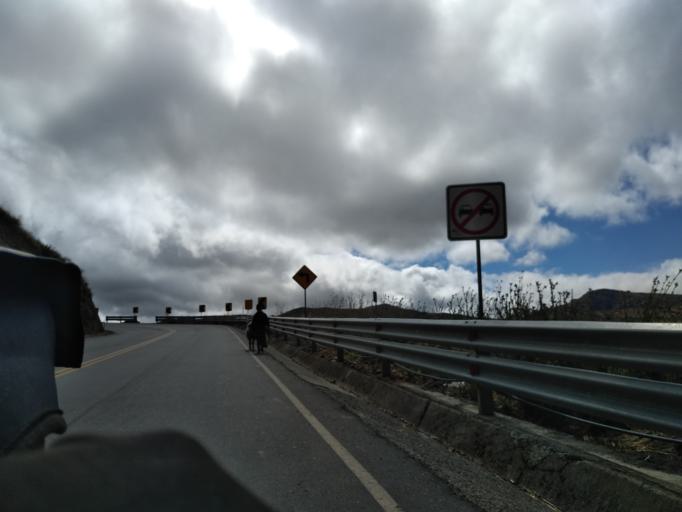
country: EC
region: Cotopaxi
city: Pujili
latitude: -0.9602
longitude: -78.9112
